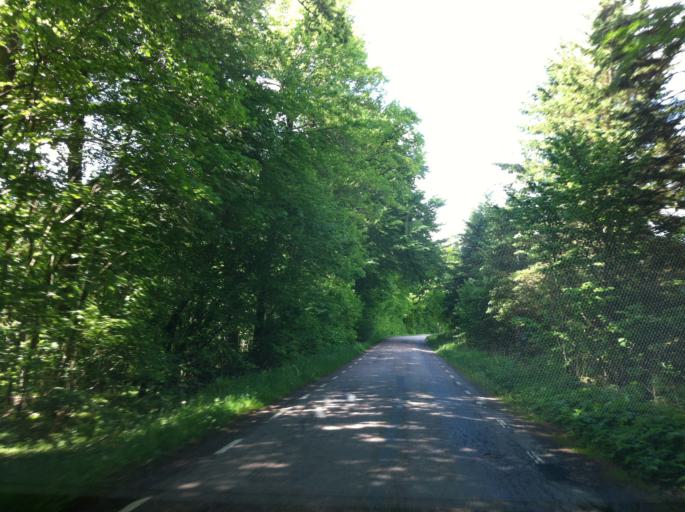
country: SE
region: Skane
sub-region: Svalovs Kommun
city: Kagerod
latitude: 55.9617
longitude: 13.0442
